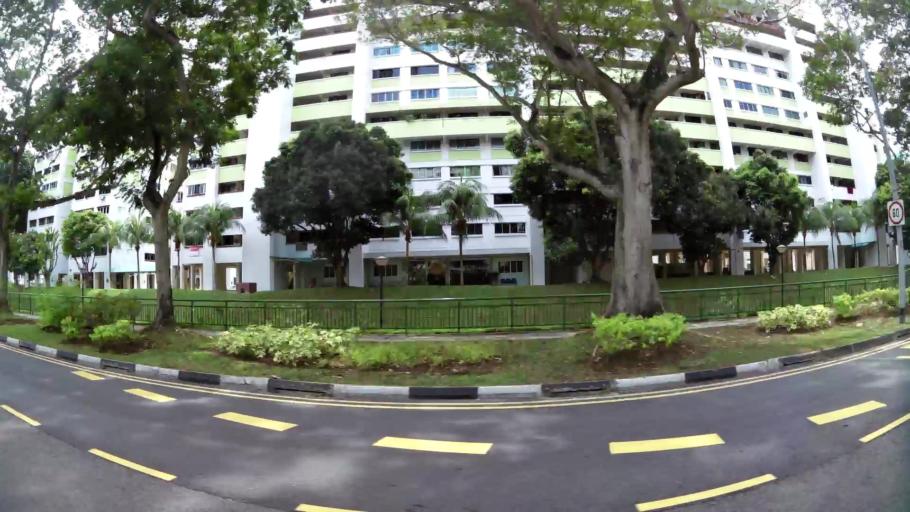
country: MY
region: Johor
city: Johor Bahru
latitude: 1.3779
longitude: 103.7709
